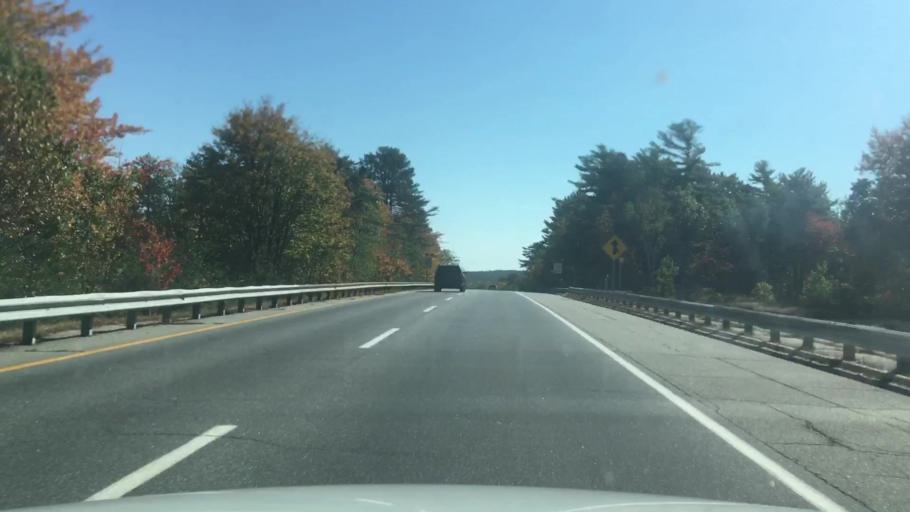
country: US
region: Maine
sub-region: Sagadahoc County
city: Bath
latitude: 43.9101
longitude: -69.8441
